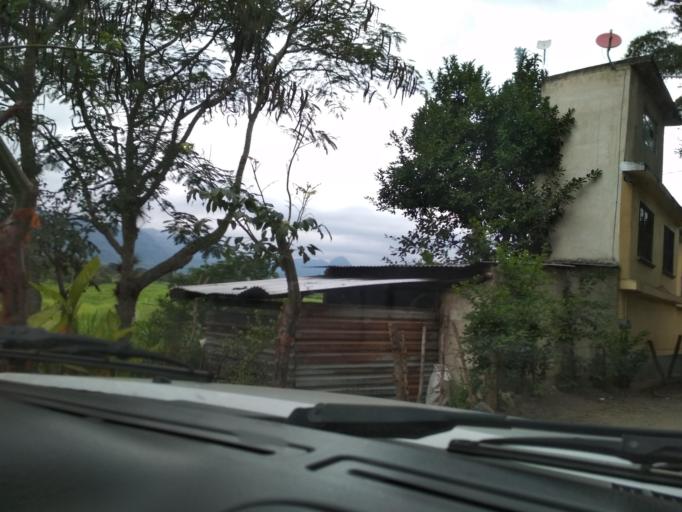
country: MX
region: Veracruz
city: El Castillo
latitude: 19.5853
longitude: -96.8407
